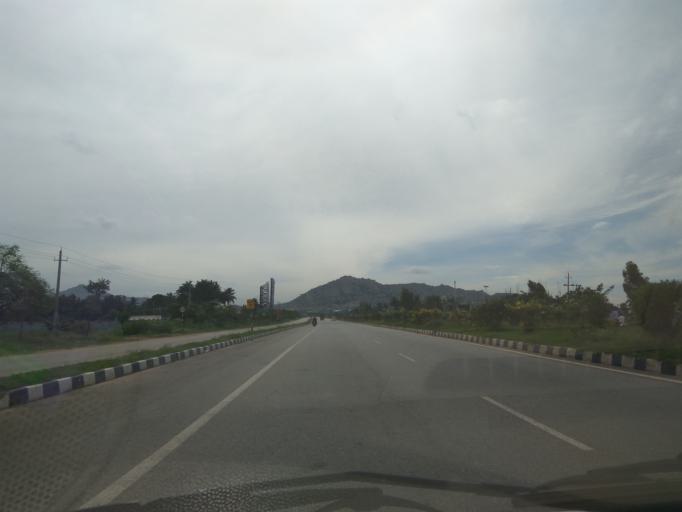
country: IN
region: Karnataka
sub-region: Kolar
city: Malur
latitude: 13.1302
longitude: 77.9888
